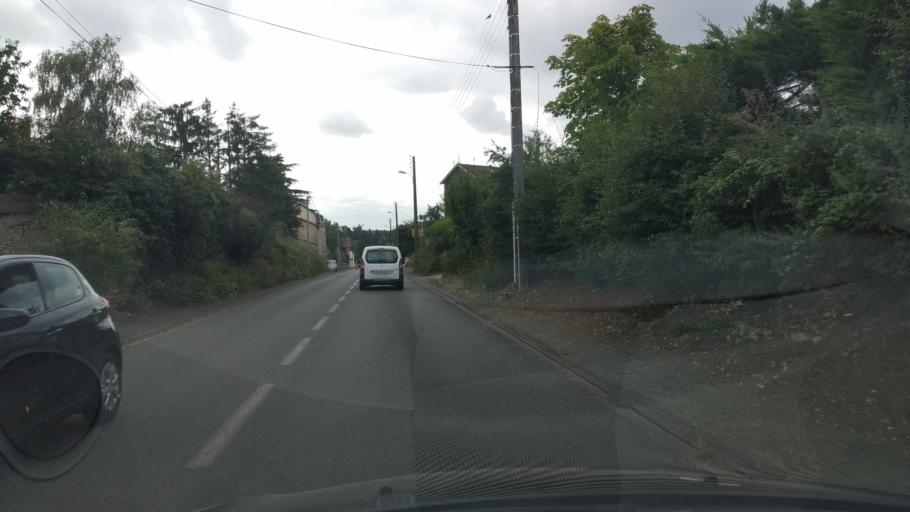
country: FR
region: Poitou-Charentes
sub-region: Departement de la Vienne
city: Saint-Benoit
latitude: 46.5616
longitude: 0.3558
